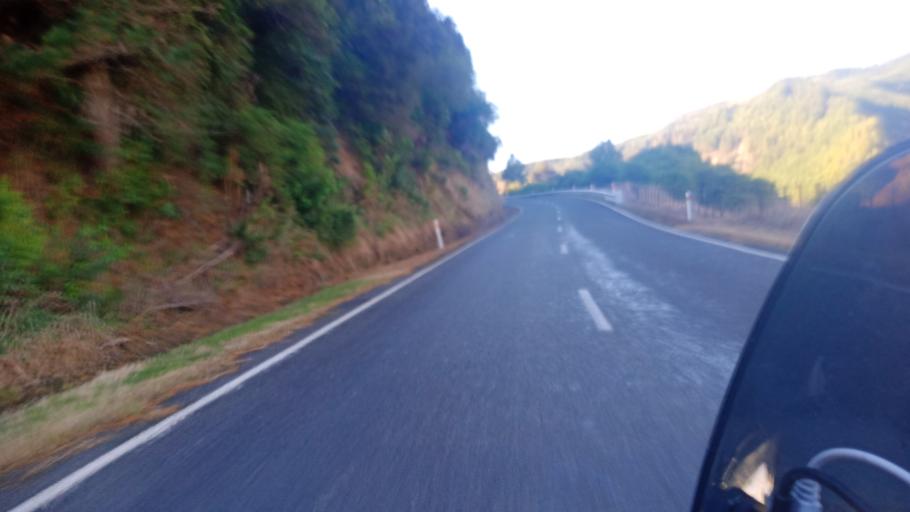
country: NZ
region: Hawke's Bay
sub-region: Wairoa District
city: Wairoa
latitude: -38.8769
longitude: 177.2241
